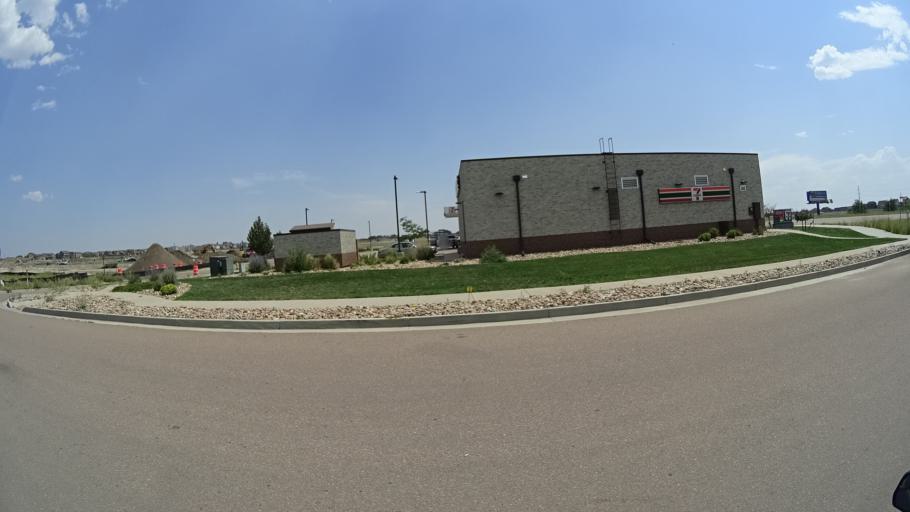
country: US
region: Colorado
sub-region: El Paso County
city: Black Forest
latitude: 38.9417
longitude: -104.6816
